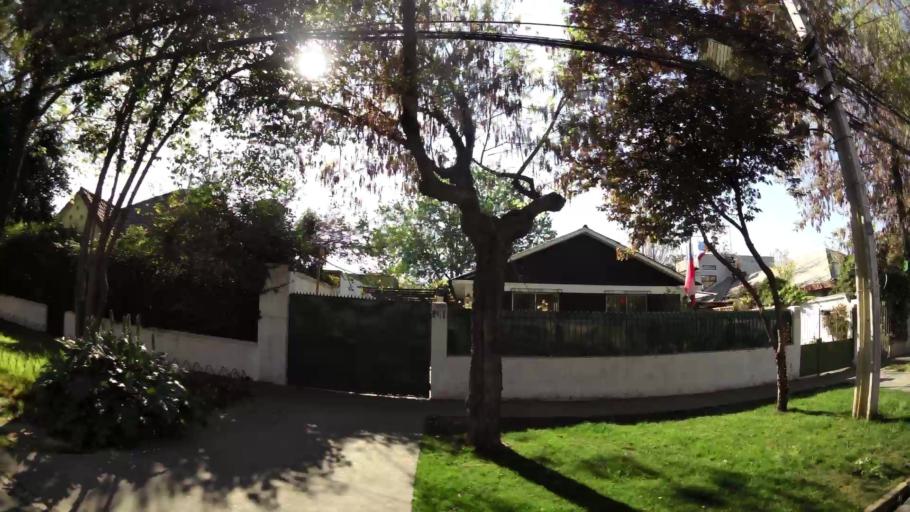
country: CL
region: Santiago Metropolitan
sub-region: Provincia de Santiago
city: Villa Presidente Frei, Nunoa, Santiago, Chile
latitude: -33.4469
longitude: -70.5809
